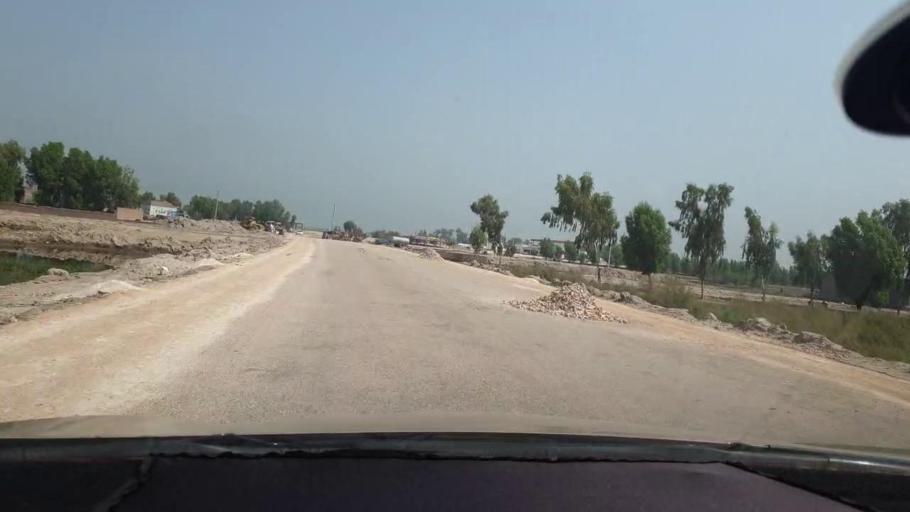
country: PK
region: Sindh
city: Kambar
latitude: 27.5860
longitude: 68.0251
